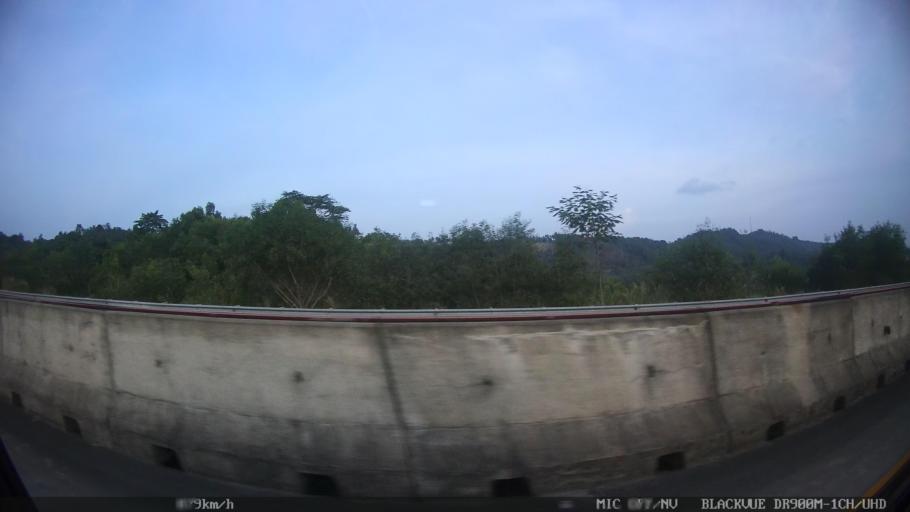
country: ID
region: Lampung
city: Penengahan
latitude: -5.8313
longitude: 105.7319
